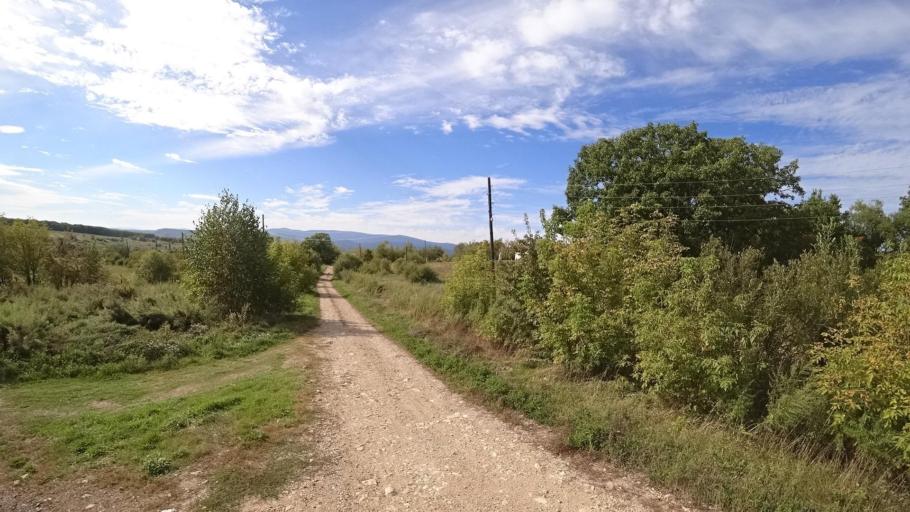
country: RU
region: Primorskiy
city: Dostoyevka
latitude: 44.3246
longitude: 133.4805
